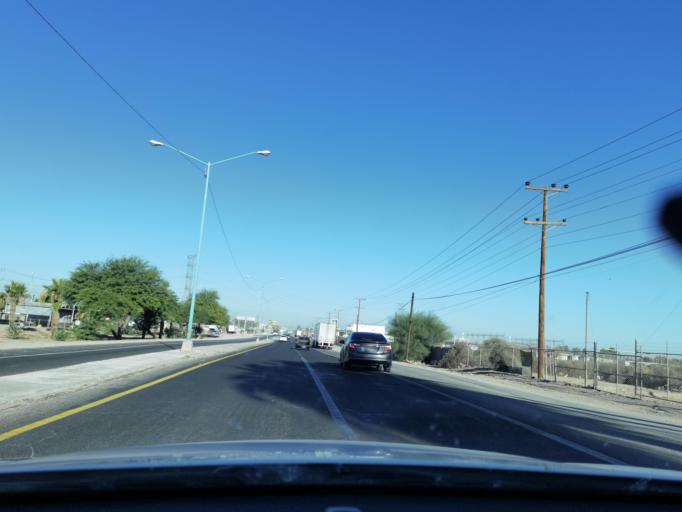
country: MX
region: Baja California
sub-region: Mexicali
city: Islas Agrarias Grupo A
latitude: 32.6529
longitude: -115.3522
